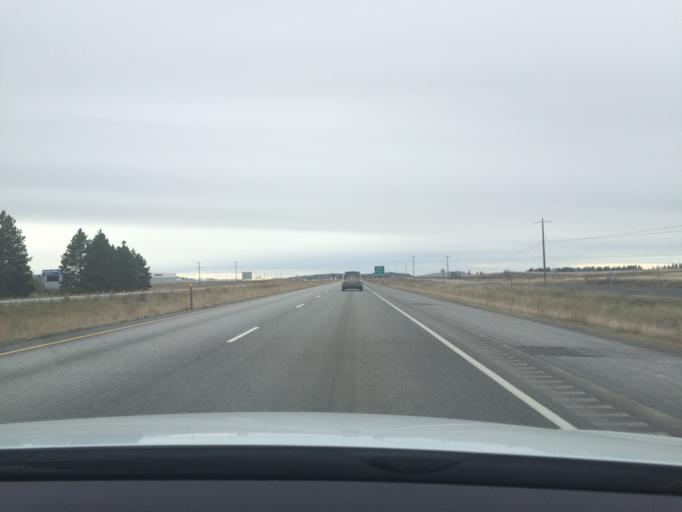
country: US
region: Washington
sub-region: Spokane County
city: Airway Heights
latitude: 47.6035
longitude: -117.5411
